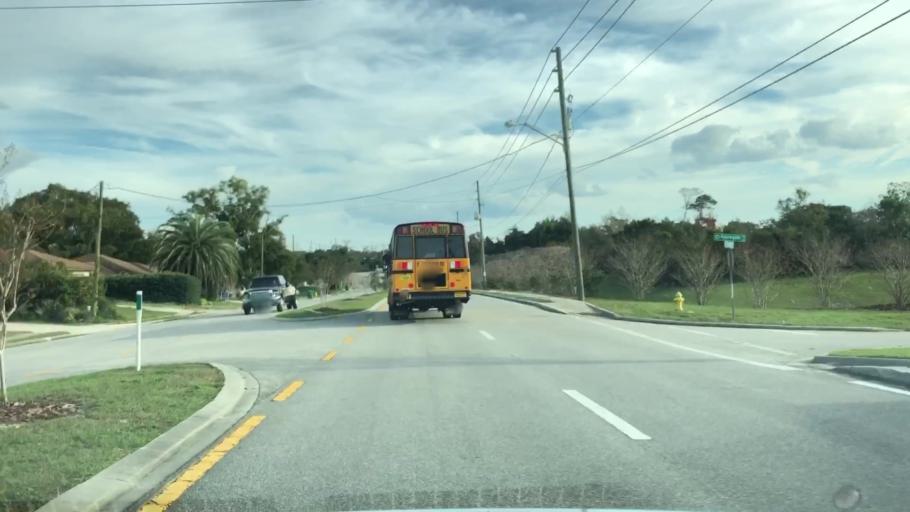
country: US
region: Florida
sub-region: Volusia County
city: Deltona
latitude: 28.9262
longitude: -81.2604
